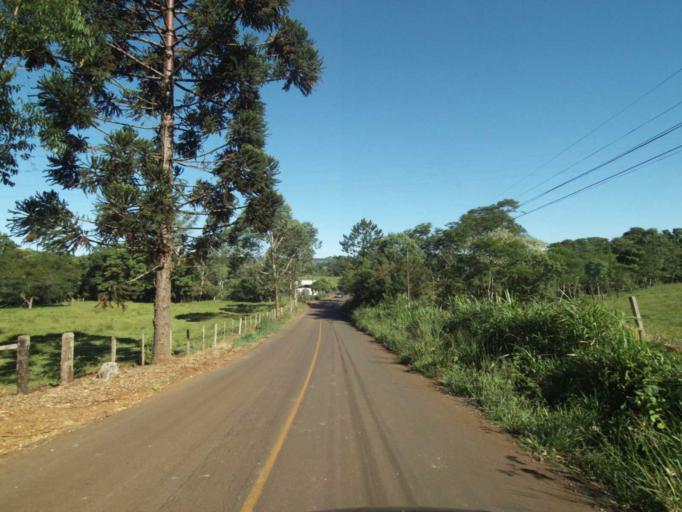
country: BR
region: Parana
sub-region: Coronel Vivida
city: Coronel Vivida
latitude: -25.9657
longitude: -52.7995
